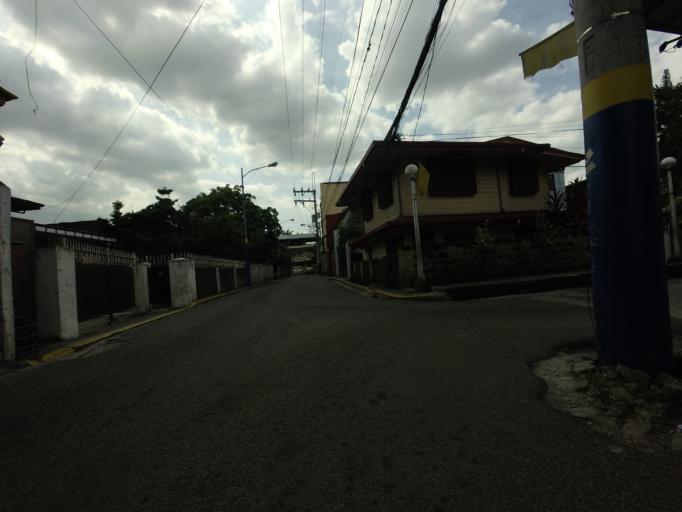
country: PH
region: Metro Manila
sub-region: San Juan
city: San Juan
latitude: 14.5864
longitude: 121.0216
